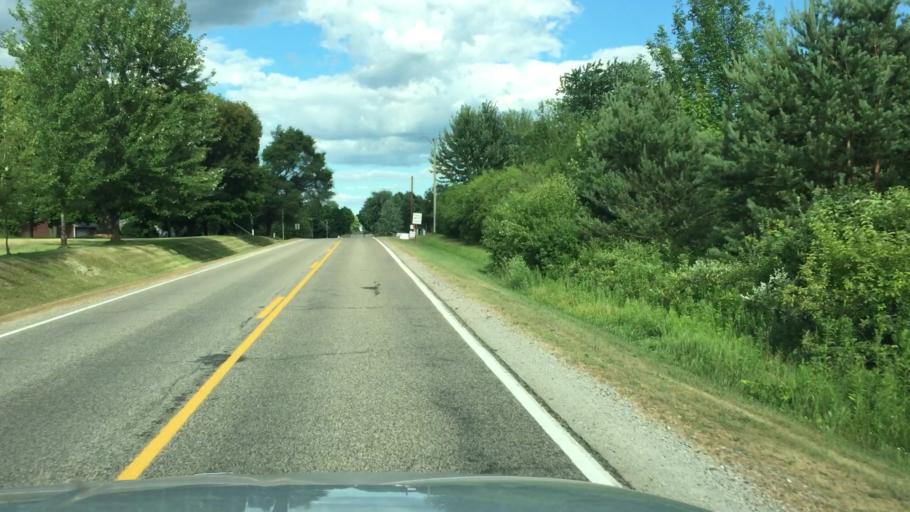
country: US
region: Michigan
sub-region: Saint Clair County
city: Yale
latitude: 43.1289
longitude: -82.8392
